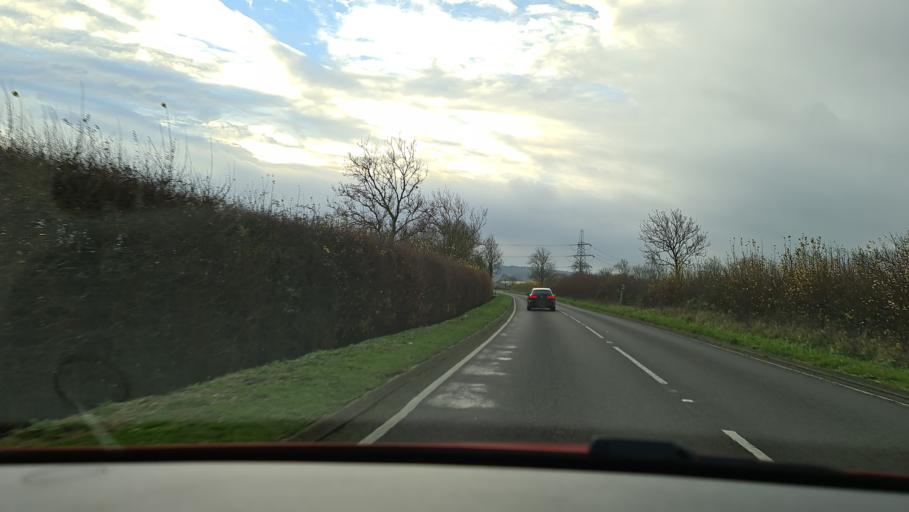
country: GB
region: England
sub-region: Oxfordshire
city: Bicester
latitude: 51.8616
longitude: -1.0914
